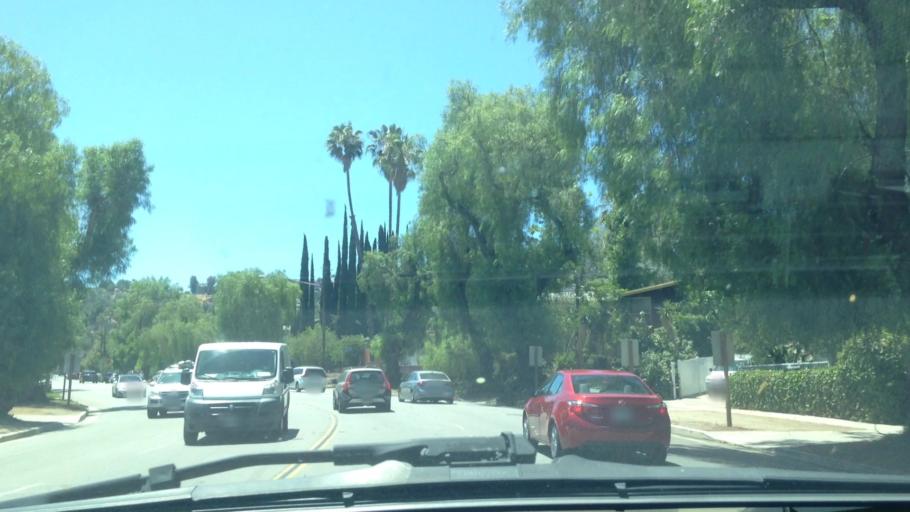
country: US
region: California
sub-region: Los Angeles County
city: Woodland Hills
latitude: 34.1539
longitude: -118.6059
